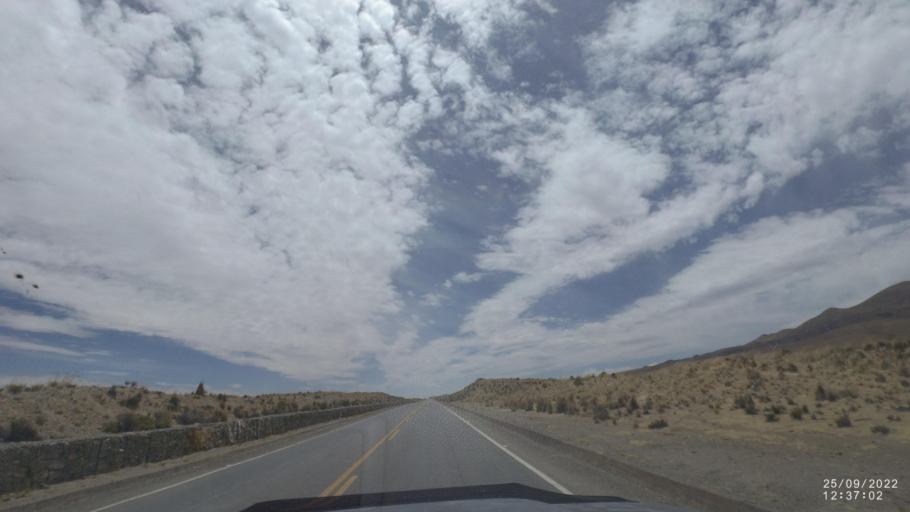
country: BO
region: Oruro
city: Machacamarca
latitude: -18.1544
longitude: -66.9869
